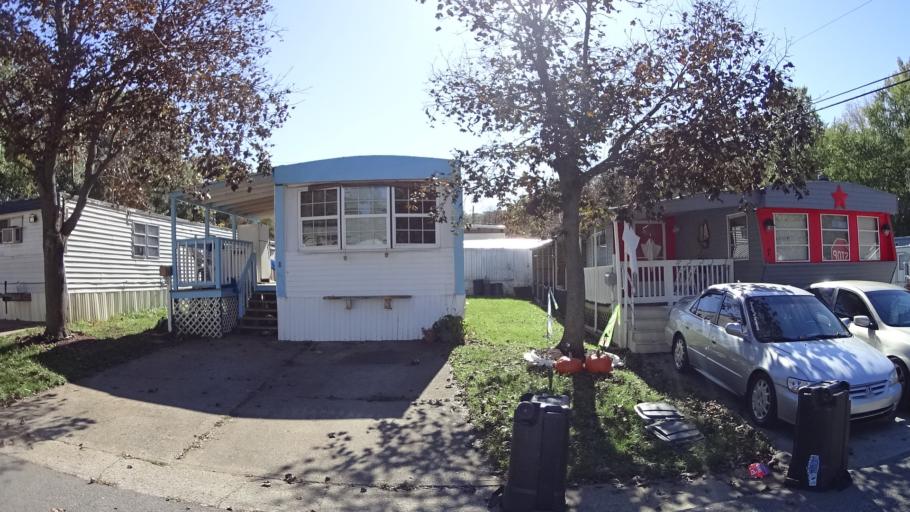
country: US
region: Ohio
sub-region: Lorain County
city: Lorain
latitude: 41.4325
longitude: -82.1670
